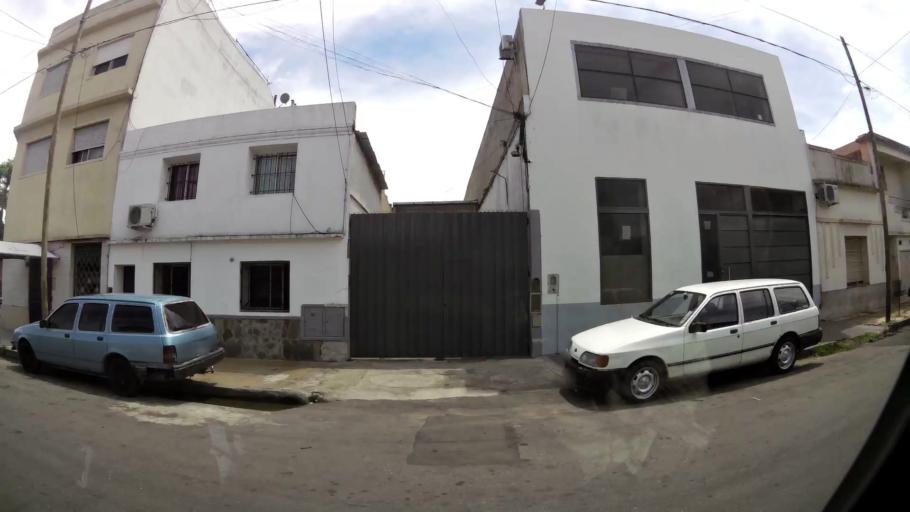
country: AR
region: Buenos Aires
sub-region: Partido de Avellaneda
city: Avellaneda
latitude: -34.6643
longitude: -58.3830
